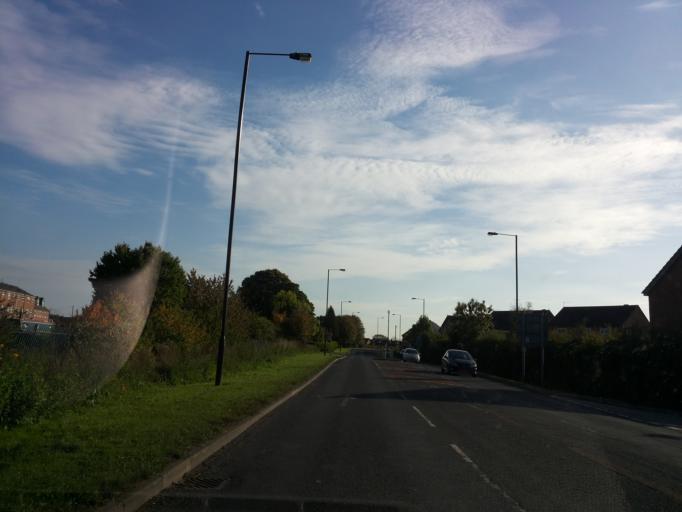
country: GB
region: England
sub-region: Doncaster
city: Hatfield
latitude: 53.6065
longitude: -0.9645
